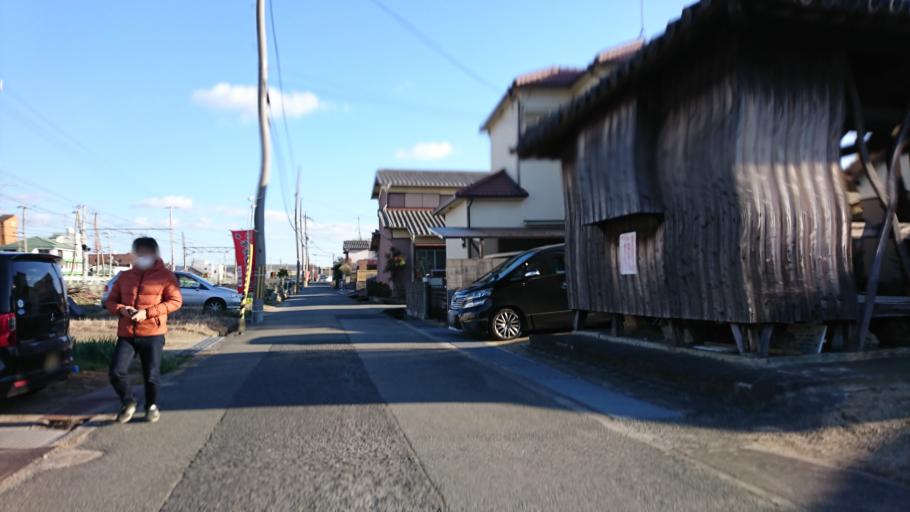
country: JP
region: Hyogo
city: Kakogawacho-honmachi
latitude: 34.7514
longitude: 134.8158
